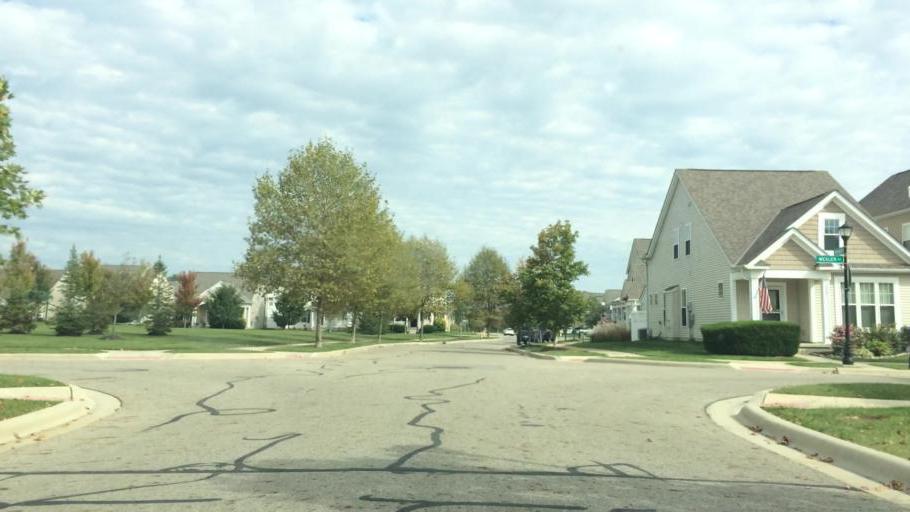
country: US
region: Ohio
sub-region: Franklin County
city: Hilliard
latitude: 40.0671
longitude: -83.1760
